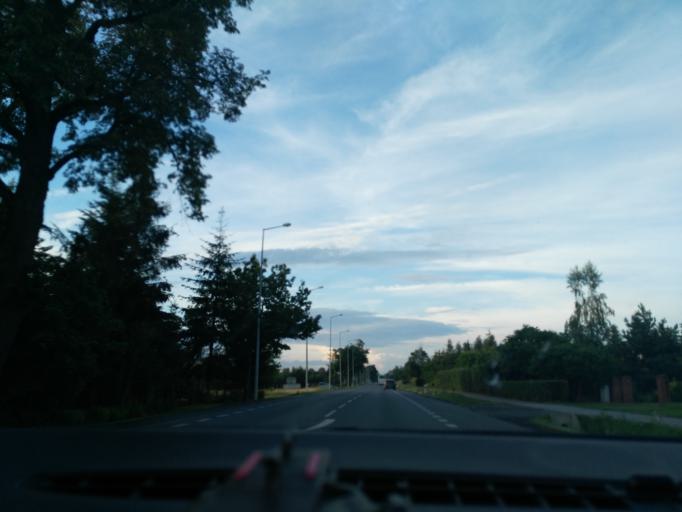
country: PL
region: Lublin Voivodeship
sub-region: Powiat lubelski
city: Niedrzwica Duza
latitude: 51.0962
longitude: 22.3685
